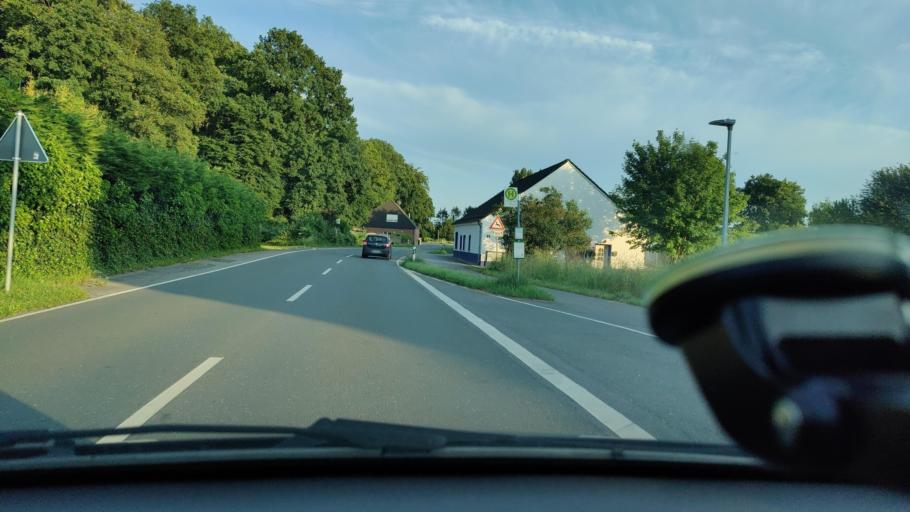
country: DE
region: North Rhine-Westphalia
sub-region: Regierungsbezirk Dusseldorf
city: Kamp-Lintfort
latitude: 51.4718
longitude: 6.5256
